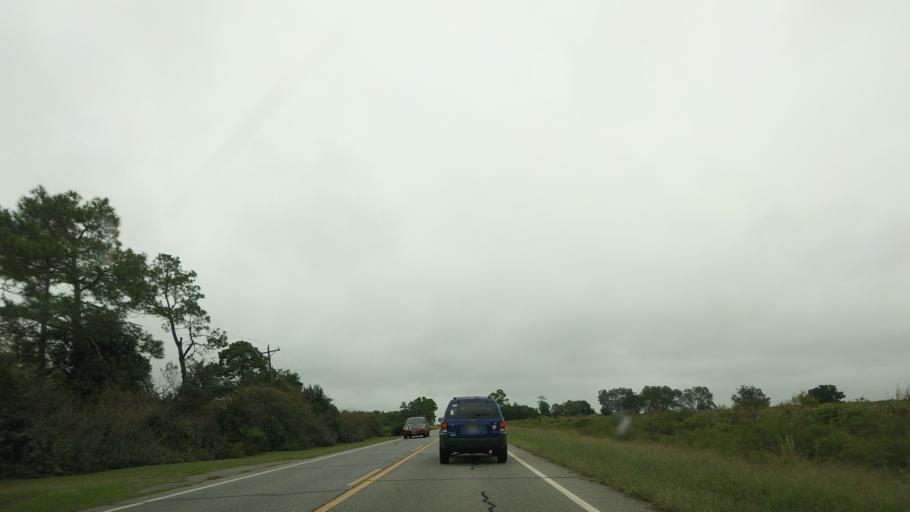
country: US
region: Georgia
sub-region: Irwin County
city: Ocilla
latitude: 31.5565
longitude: -83.2533
